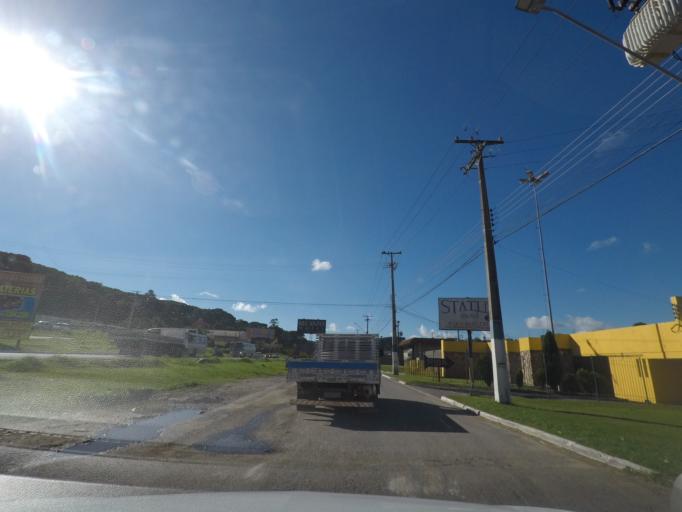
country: BR
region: Parana
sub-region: Almirante Tamandare
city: Almirante Tamandare
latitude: -25.3439
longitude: -49.2831
